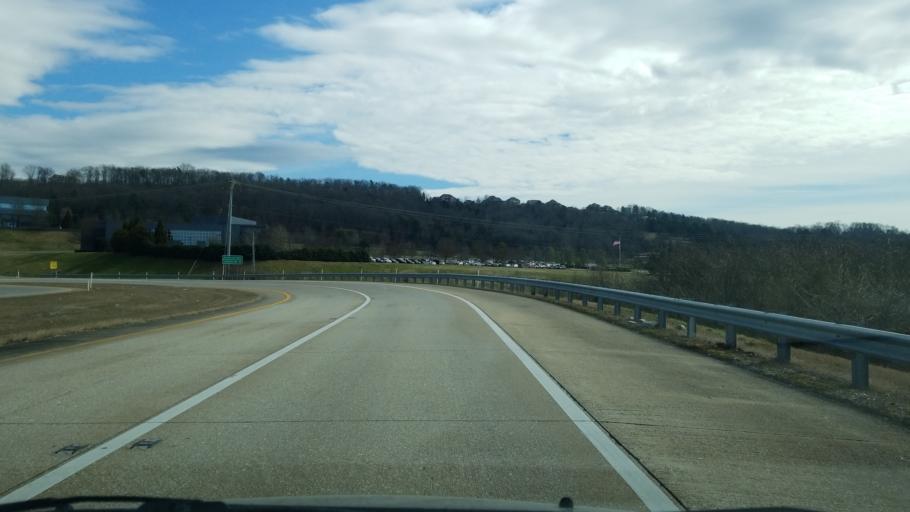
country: US
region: Tennessee
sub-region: Hamilton County
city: Harrison
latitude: 35.0576
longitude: -85.1314
